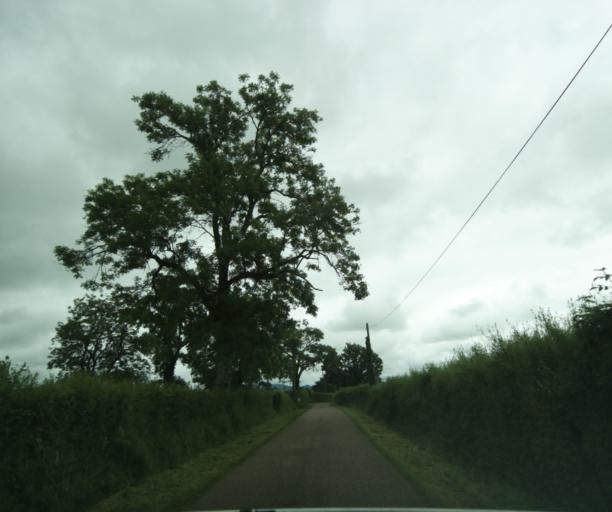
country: FR
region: Bourgogne
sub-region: Departement de Saone-et-Loire
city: Charolles
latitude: 46.4603
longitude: 4.2931
